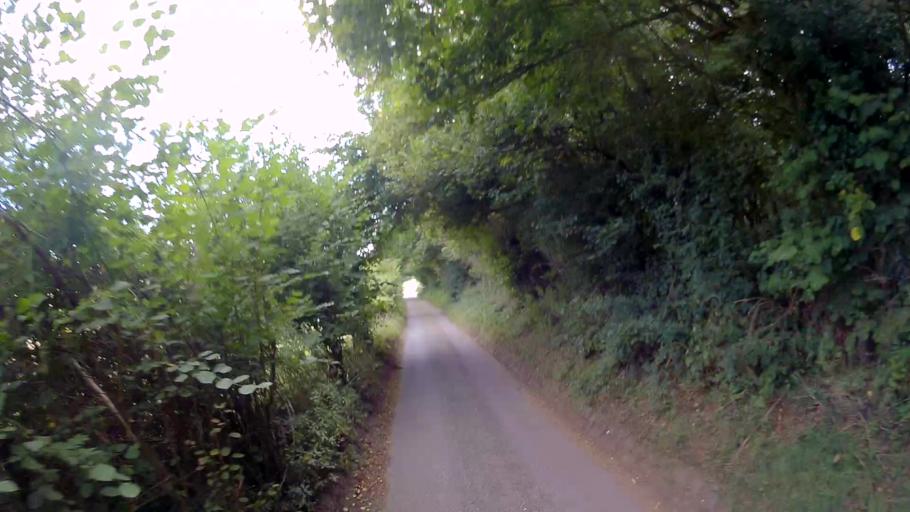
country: GB
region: England
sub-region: Hampshire
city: Odiham
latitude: 51.2390
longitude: -0.9739
